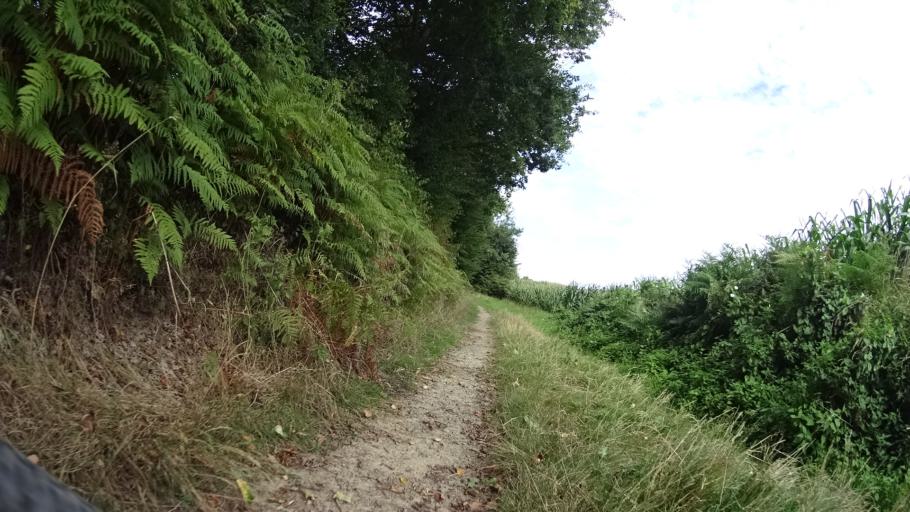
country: FR
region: Brittany
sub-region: Departement d'Ille-et-Vilaine
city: La Meziere
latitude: 48.2226
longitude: -1.7400
